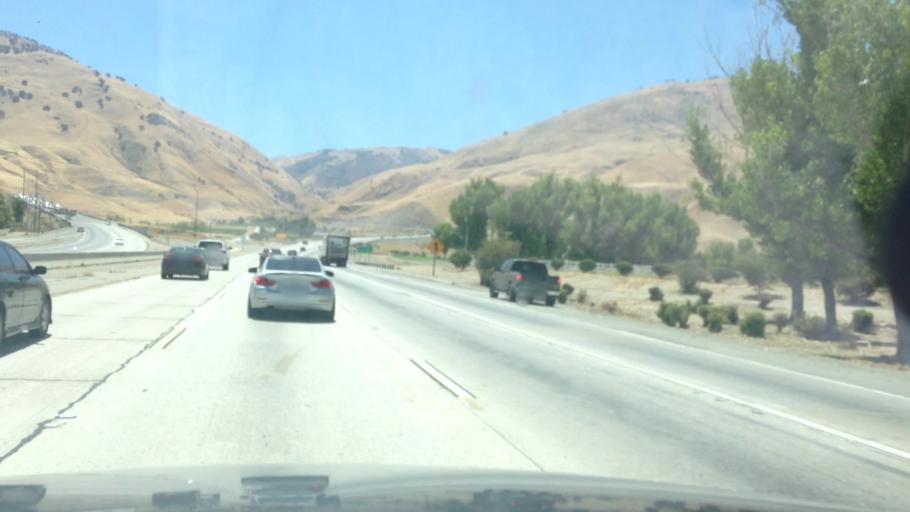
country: US
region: California
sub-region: Kern County
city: Frazier Park
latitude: 34.9432
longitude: -118.9318
